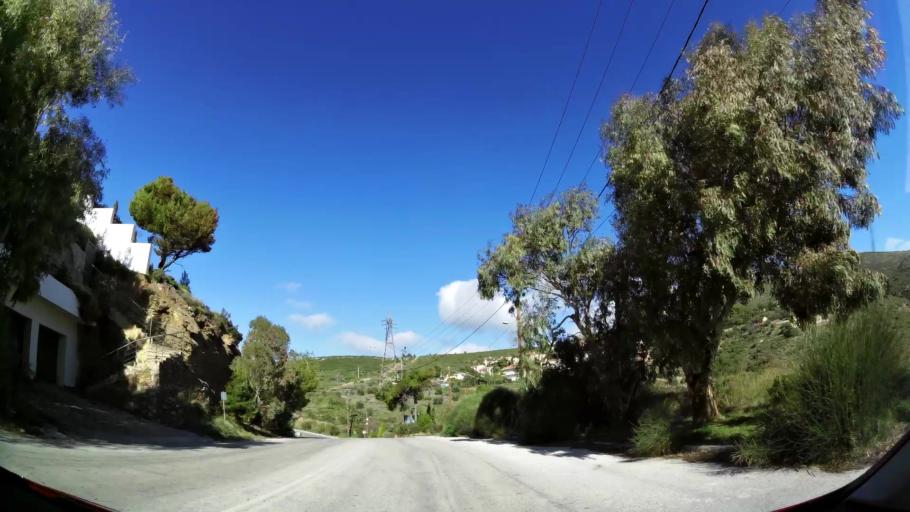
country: GR
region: Attica
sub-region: Nomarchia Anatolikis Attikis
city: Dhrafi
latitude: 38.0443
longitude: 23.8933
